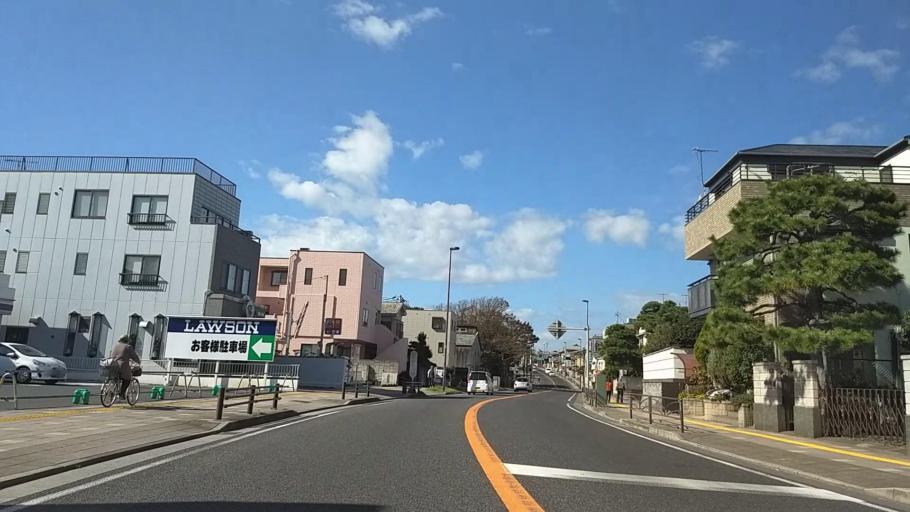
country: JP
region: Kanagawa
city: Oiso
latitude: 35.3074
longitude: 139.3128
